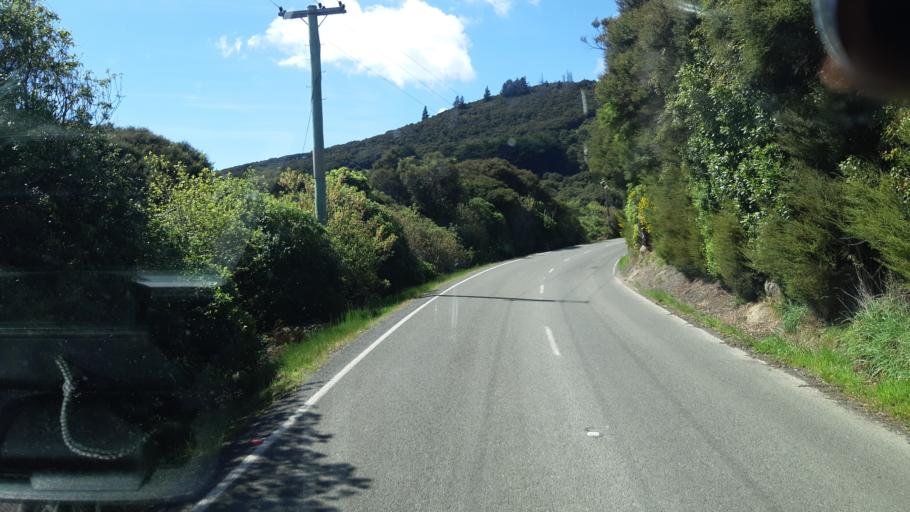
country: NZ
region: Otago
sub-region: Dunedin City
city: Portobello
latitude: -45.7791
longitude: 170.5959
